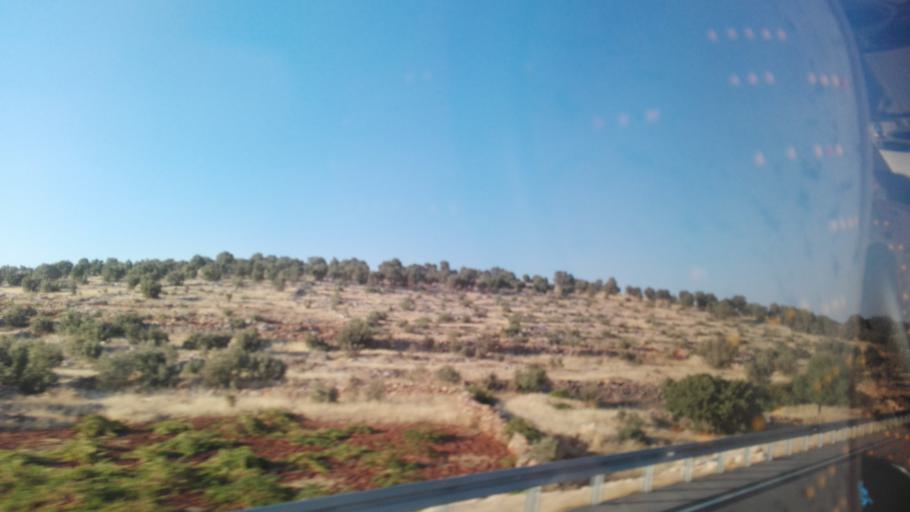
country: TR
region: Mardin
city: Ortaca
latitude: 37.5226
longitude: 41.5898
